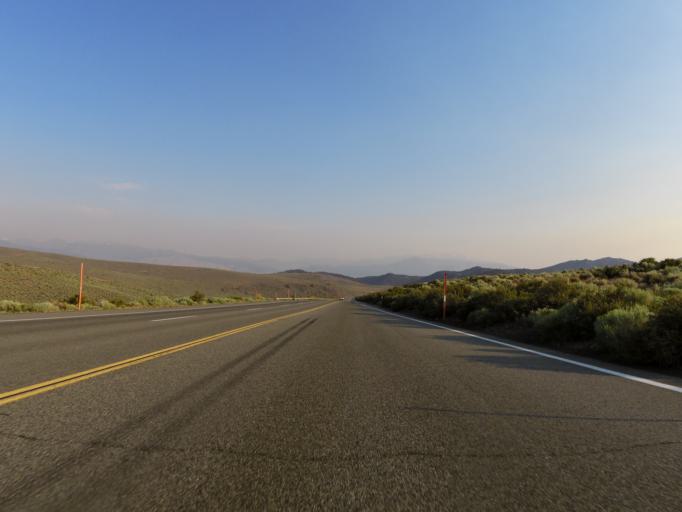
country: US
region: California
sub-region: Mono County
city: Bridgeport
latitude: 38.1592
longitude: -119.1881
